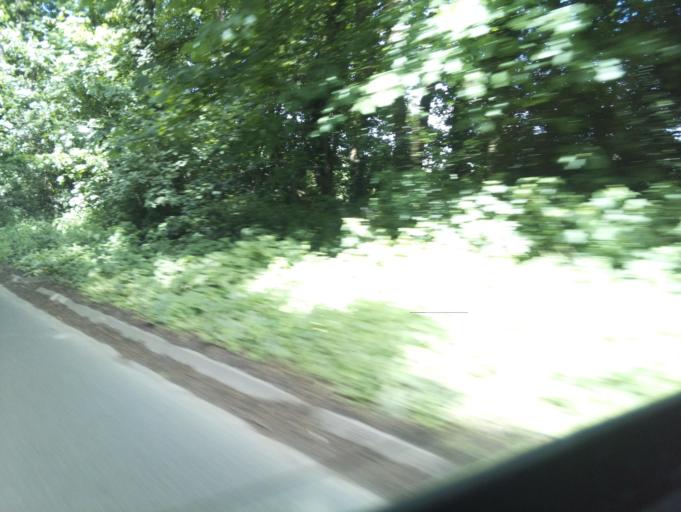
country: GB
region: England
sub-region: Devon
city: Uffculme
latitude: 50.8515
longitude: -3.3280
